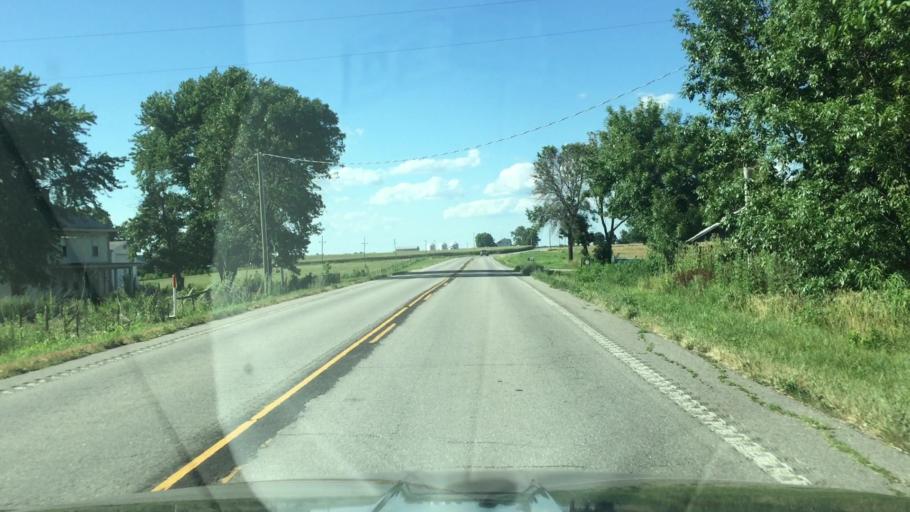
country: US
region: Missouri
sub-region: Moniteau County
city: Tipton
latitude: 38.6061
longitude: -92.7900
